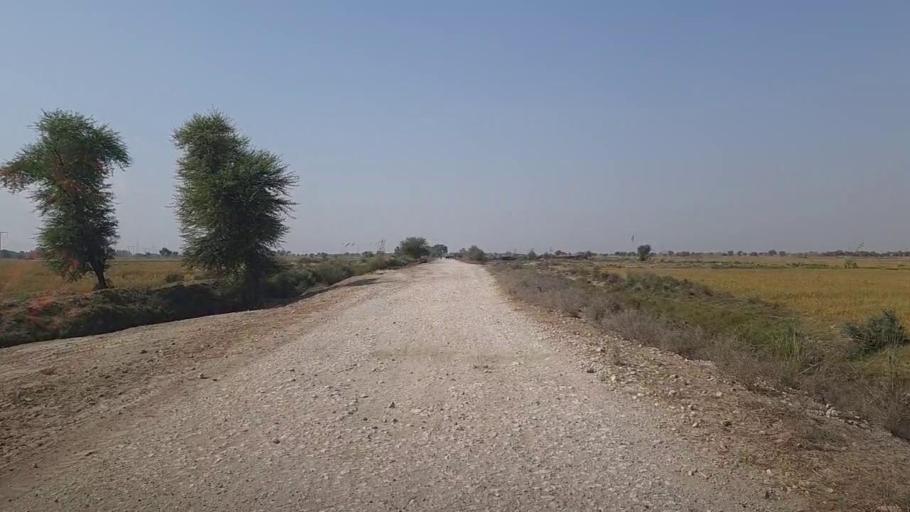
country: PK
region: Sindh
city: Kandhkot
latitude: 28.3891
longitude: 69.2907
